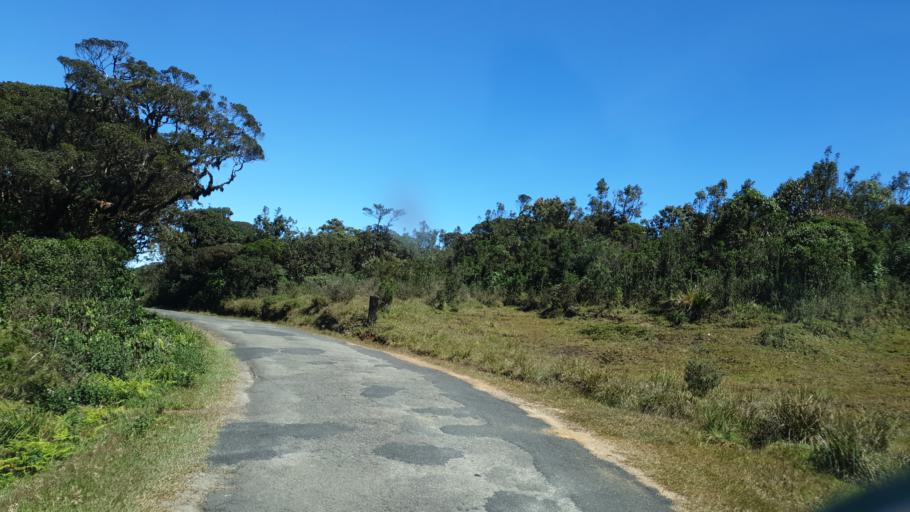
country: LK
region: Central
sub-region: Nuwara Eliya District
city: Nuwara Eliya
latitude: 6.8375
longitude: 80.8110
